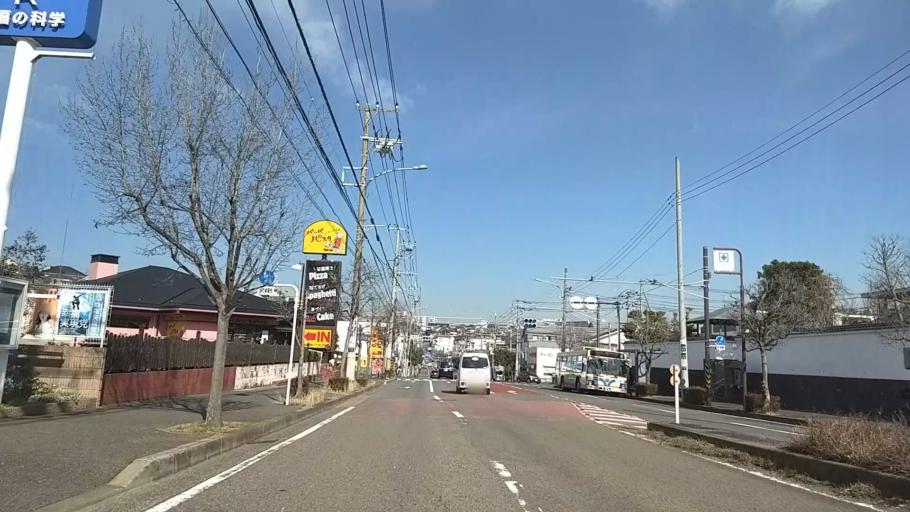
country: JP
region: Kanagawa
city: Kamakura
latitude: 35.3792
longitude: 139.5795
